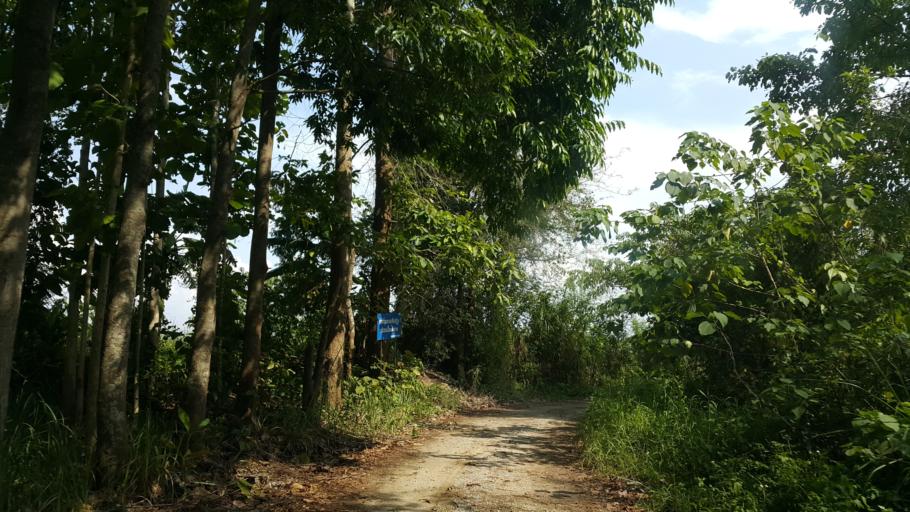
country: TH
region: Chiang Rai
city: Wiang Chai
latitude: 19.9314
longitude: 99.9326
